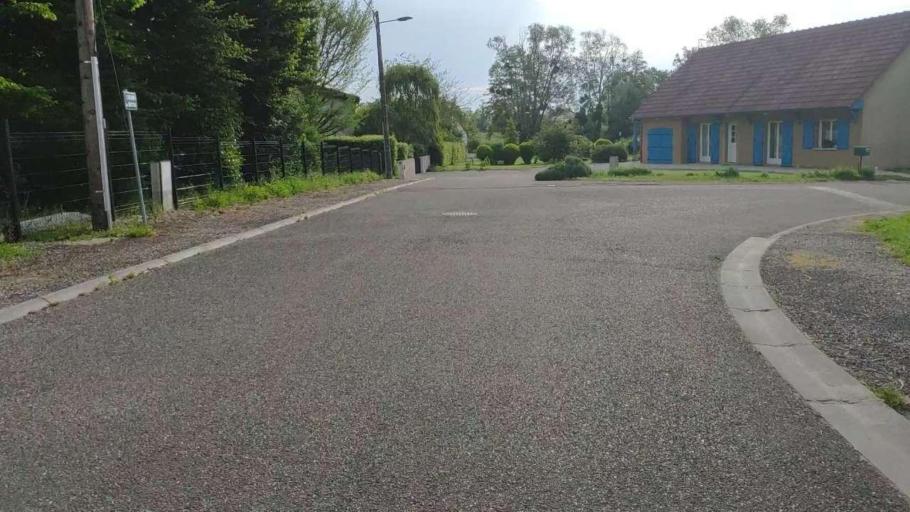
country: FR
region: Franche-Comte
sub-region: Departement du Jura
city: Bletterans
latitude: 46.7484
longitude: 5.4496
